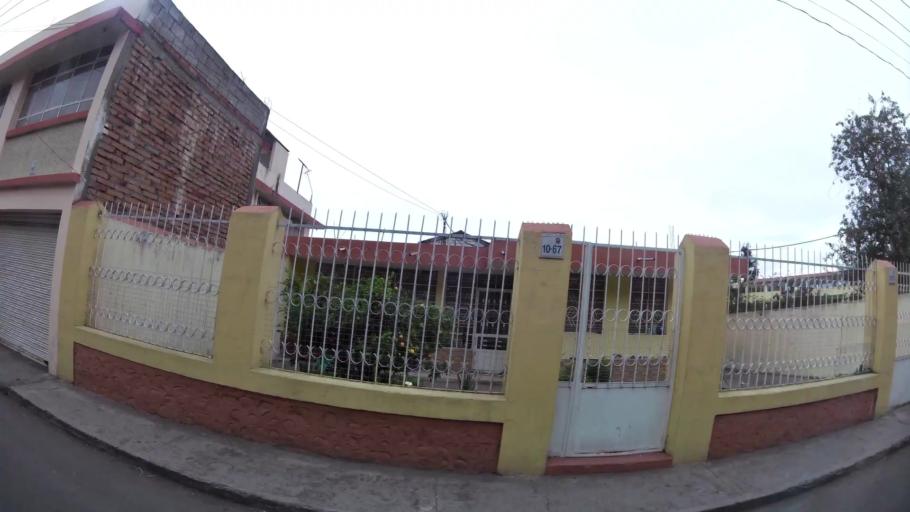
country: EC
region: Cotopaxi
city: Latacunga
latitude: -0.9306
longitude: -78.6121
